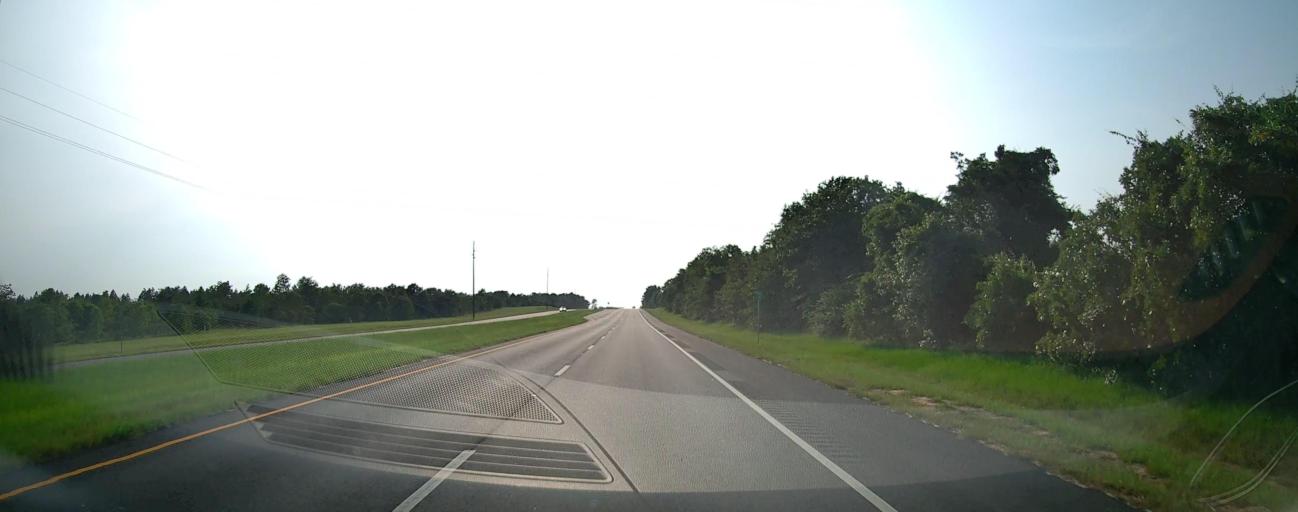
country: US
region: Georgia
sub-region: Taylor County
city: Butler
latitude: 32.5854
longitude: -84.3411
